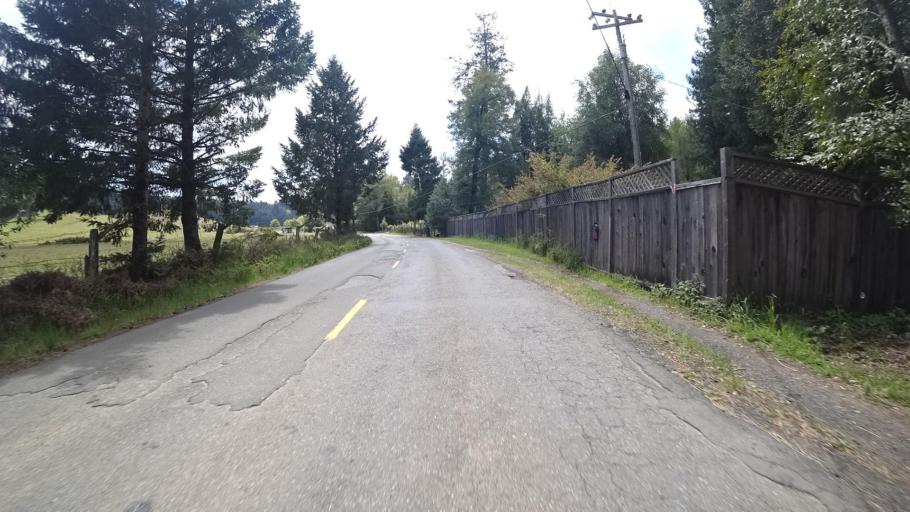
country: US
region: California
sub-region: Humboldt County
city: Redway
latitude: 40.0425
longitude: -123.9593
